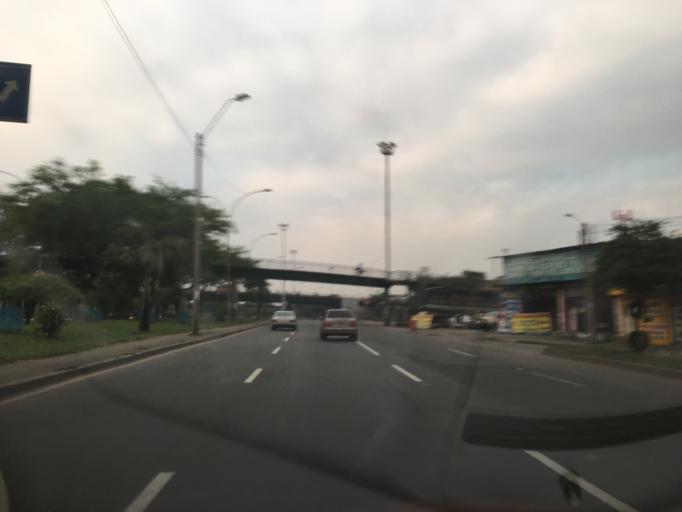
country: CO
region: Valle del Cauca
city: Cali
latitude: 3.4465
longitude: -76.5184
